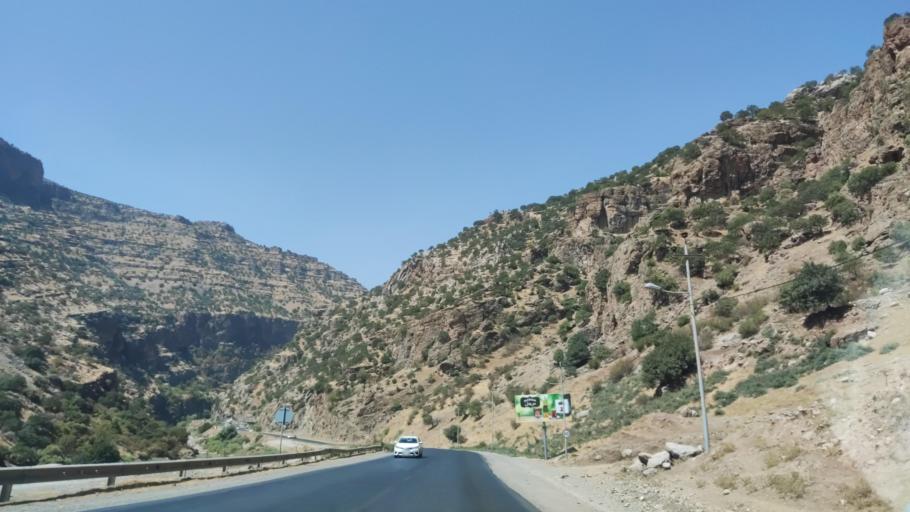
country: IQ
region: Arbil
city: Ruwandiz
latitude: 36.6309
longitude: 44.4762
